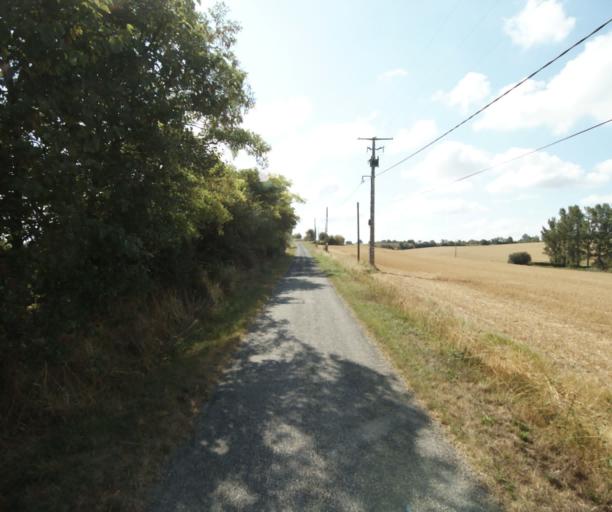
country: FR
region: Midi-Pyrenees
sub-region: Departement de la Haute-Garonne
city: Avignonet-Lauragais
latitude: 43.4379
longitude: 1.7886
